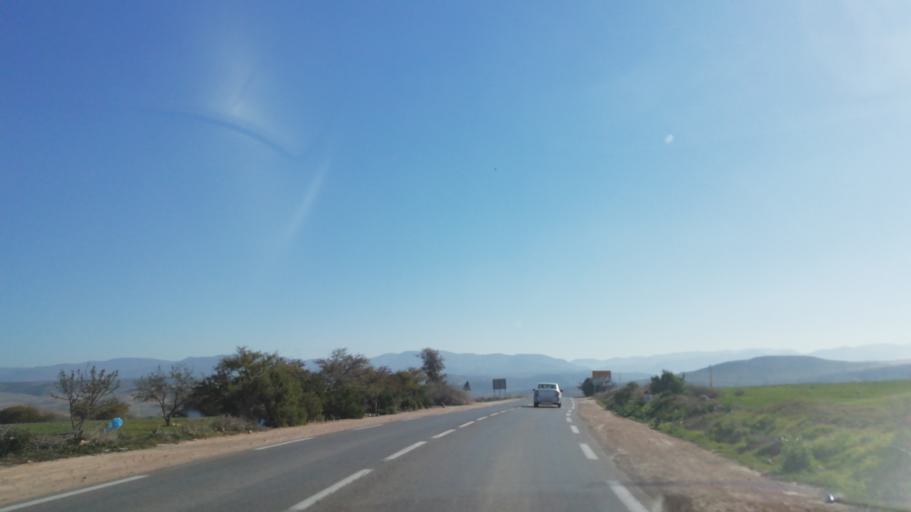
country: DZ
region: Tlemcen
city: Nedroma
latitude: 34.8324
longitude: -1.6766
